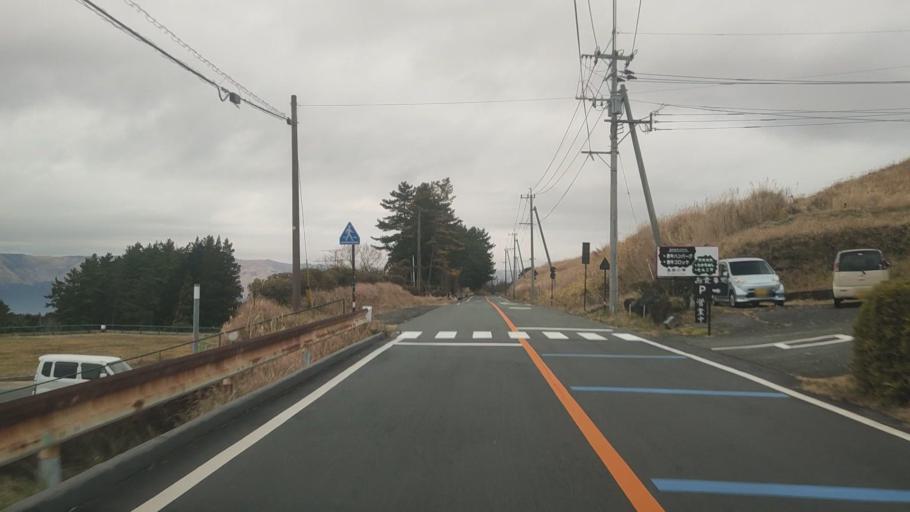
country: JP
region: Kumamoto
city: Aso
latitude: 32.8917
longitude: 131.0275
